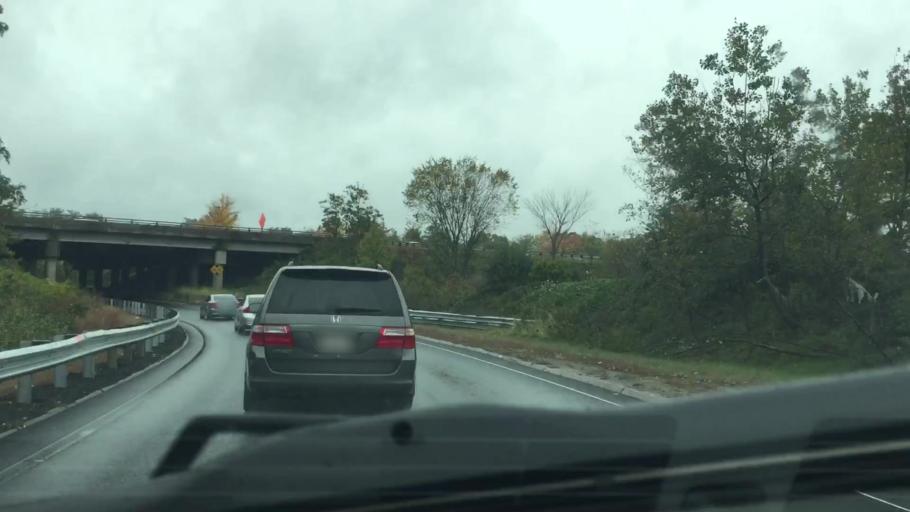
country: US
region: Massachusetts
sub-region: Essex County
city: Methuen
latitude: 42.7337
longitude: -71.2003
